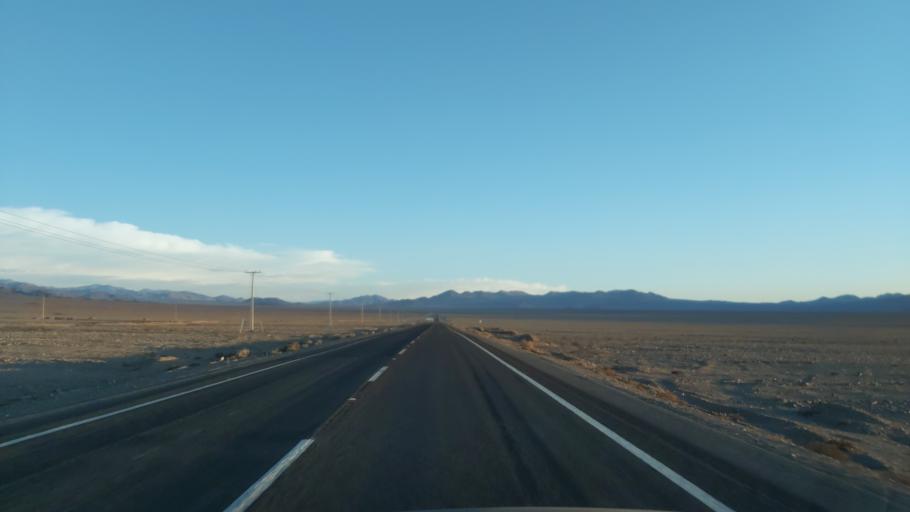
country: CL
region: Atacama
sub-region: Provincia de Chanaral
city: Diego de Almagro
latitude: -26.6214
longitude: -69.9516
